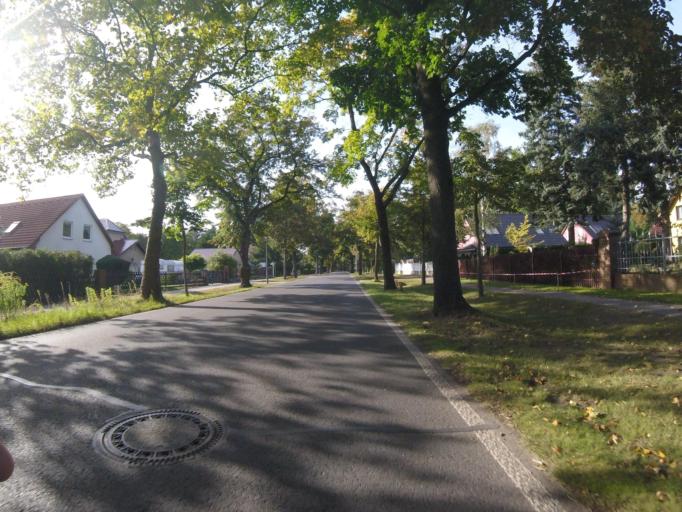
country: DE
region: Brandenburg
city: Konigs Wusterhausen
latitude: 52.2981
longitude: 13.6681
